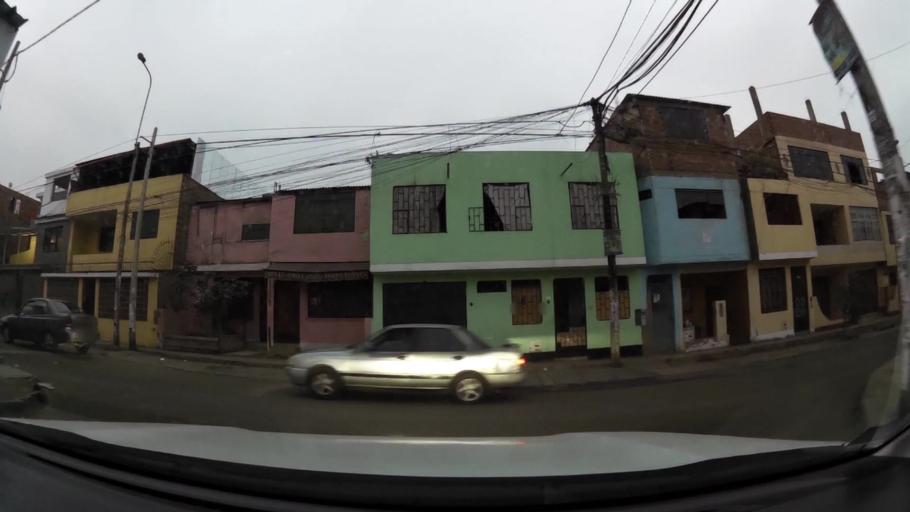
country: PE
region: Lima
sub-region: Lima
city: Surco
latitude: -12.1490
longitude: -76.9720
